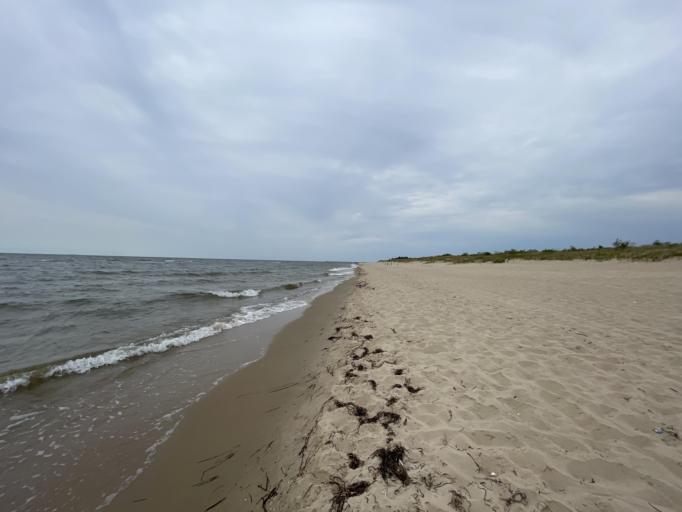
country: PL
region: Pomeranian Voivodeship
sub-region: Gdansk
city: Gdansk
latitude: 54.3737
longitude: 18.7440
